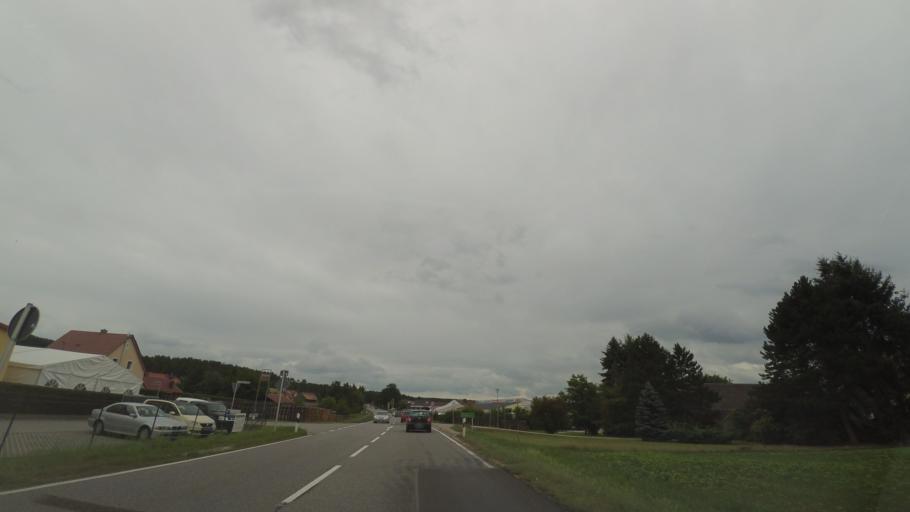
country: DE
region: Bavaria
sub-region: Upper Palatinate
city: Steinberg
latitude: 49.2917
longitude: 12.1939
